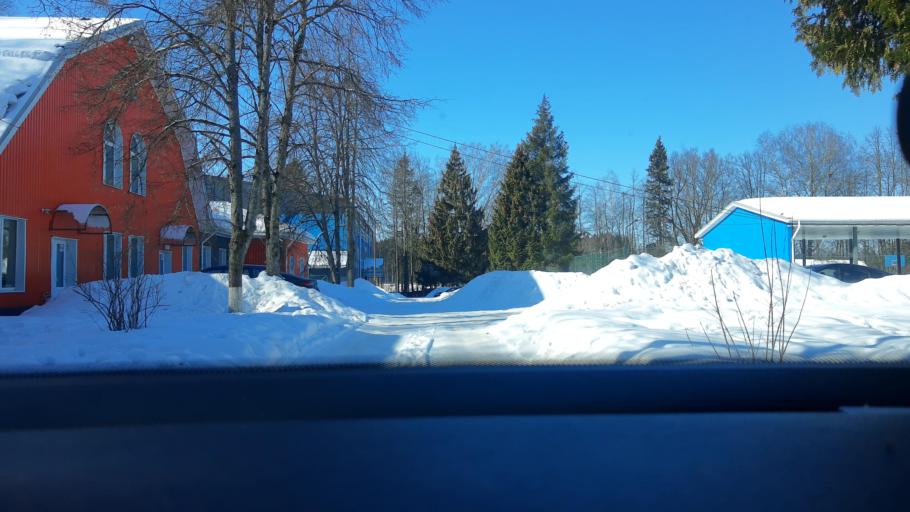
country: RU
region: Moskovskaya
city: Ivanteyevka
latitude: 55.9889
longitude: 37.9473
